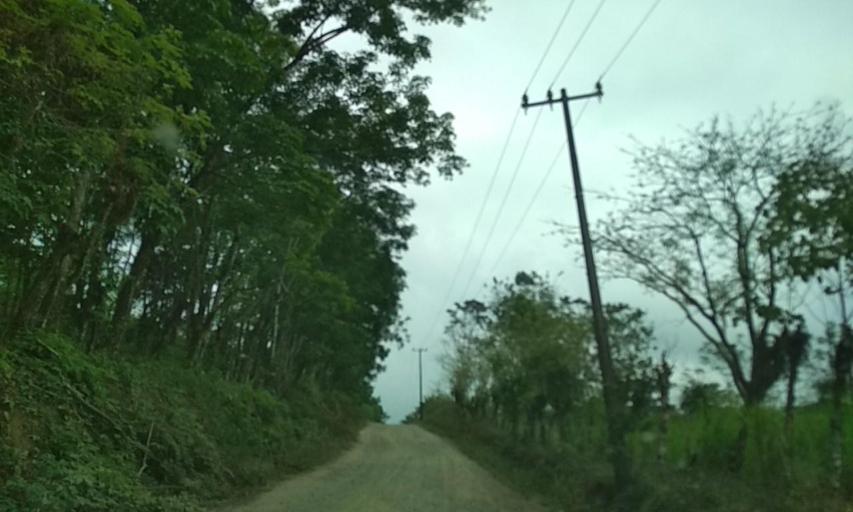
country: MX
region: Veracruz
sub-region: Uxpanapa
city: Poblado 10
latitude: 17.4885
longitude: -94.1281
